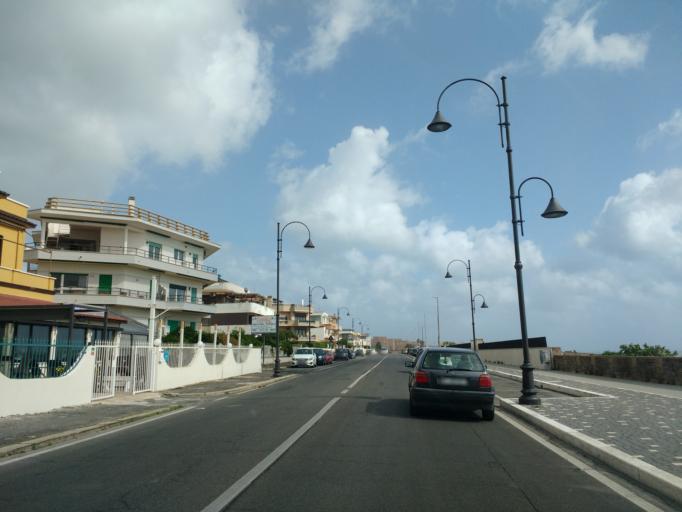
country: IT
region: Latium
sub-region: Citta metropolitana di Roma Capitale
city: Anzio
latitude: 41.4584
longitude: 12.6146
